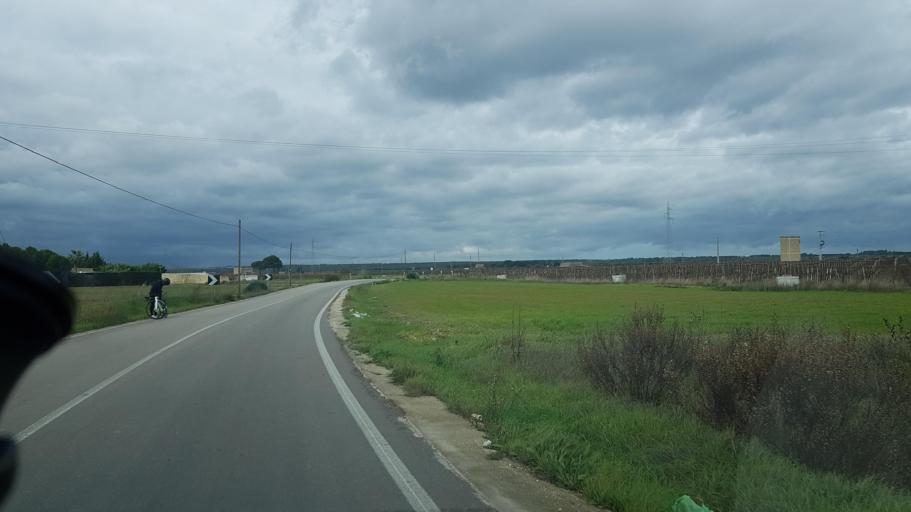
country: IT
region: Apulia
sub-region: Provincia di Brindisi
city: Francavilla Fontana
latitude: 40.5396
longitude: 17.5674
